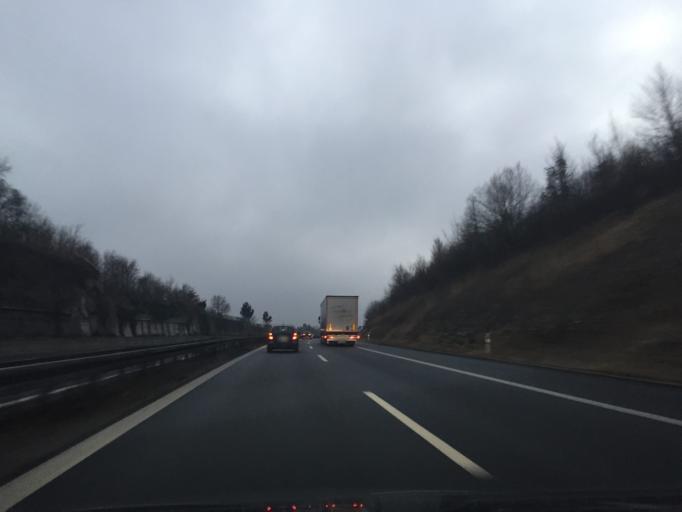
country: DE
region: Bavaria
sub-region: Upper Bavaria
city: Windach
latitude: 48.0675
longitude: 11.0238
